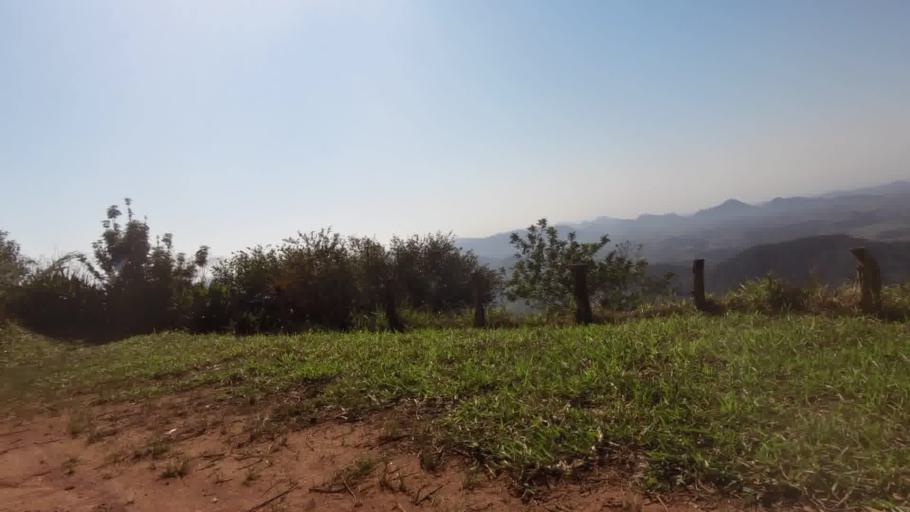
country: BR
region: Espirito Santo
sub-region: Alfredo Chaves
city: Alfredo Chaves
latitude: -20.6722
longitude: -40.7806
